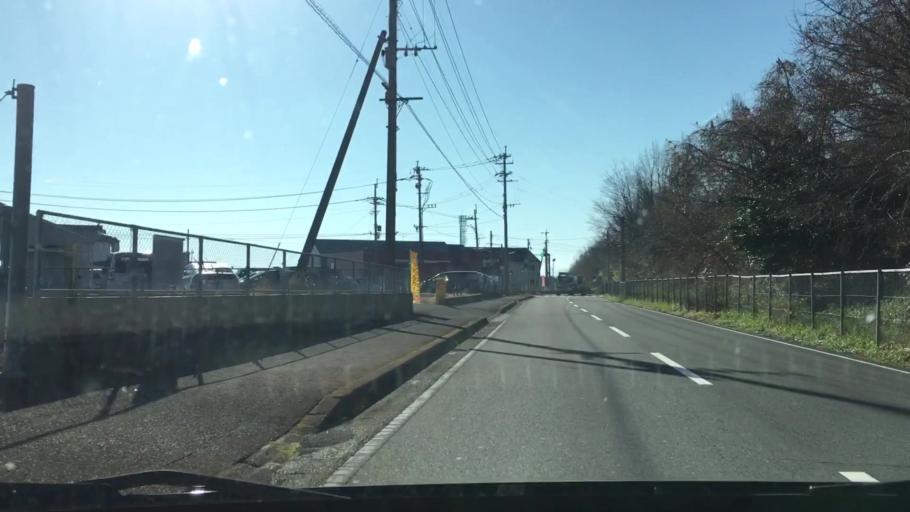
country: JP
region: Kagoshima
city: Kajiki
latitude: 31.7945
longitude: 130.7165
